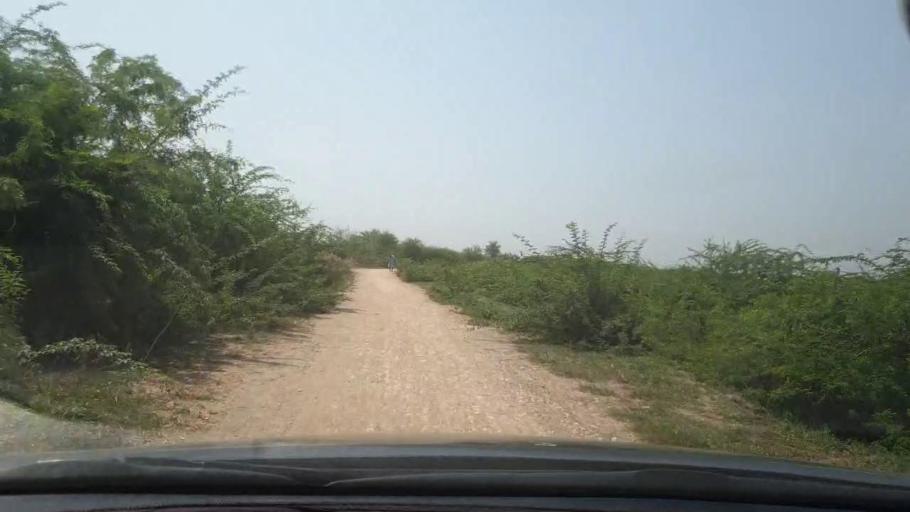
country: PK
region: Sindh
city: Tando Bago
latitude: 24.7759
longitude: 69.1833
